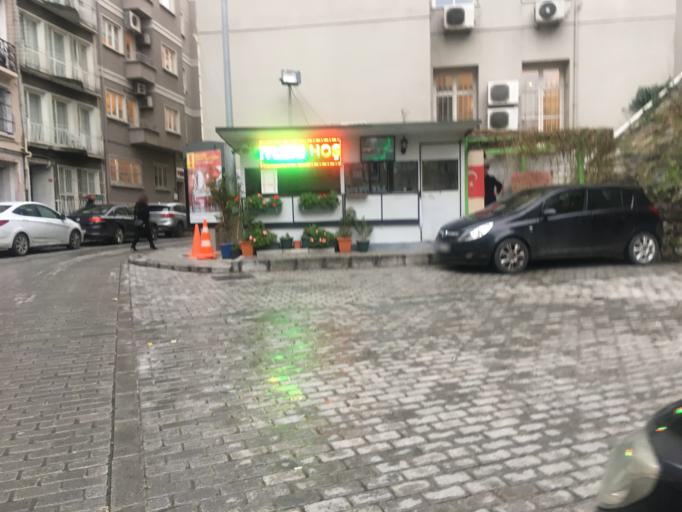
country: TR
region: Istanbul
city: Eminoenue
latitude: 41.0318
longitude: 28.9792
